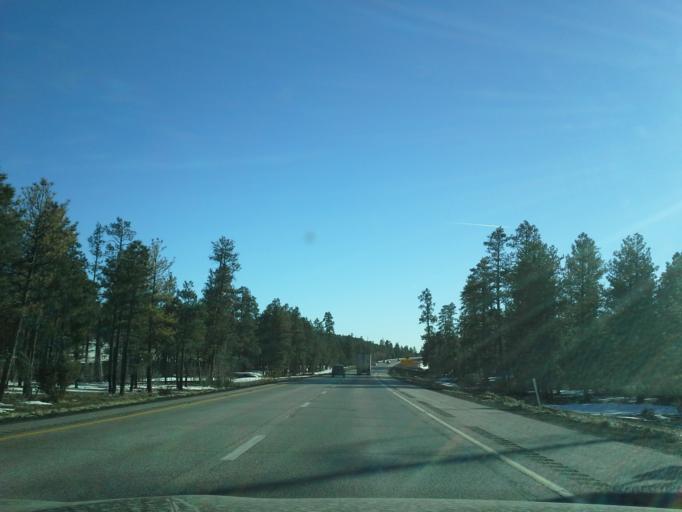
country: US
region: Arizona
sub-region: Coconino County
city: Sedona
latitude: 34.8349
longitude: -111.6055
